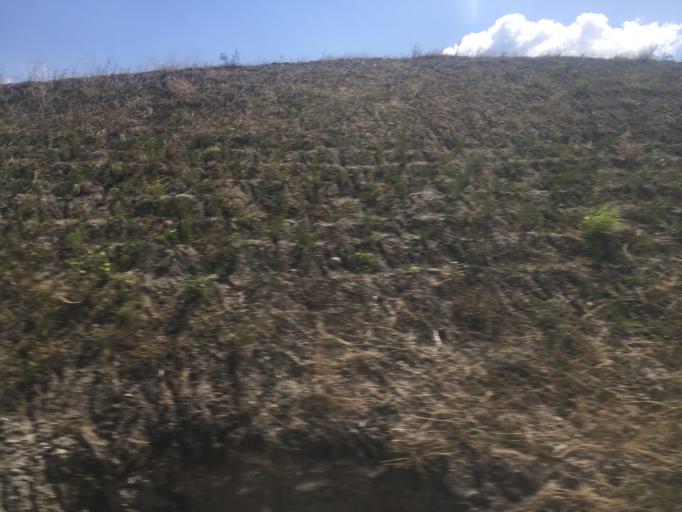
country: TR
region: Balikesir
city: Gobel
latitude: 39.9692
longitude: 28.1588
